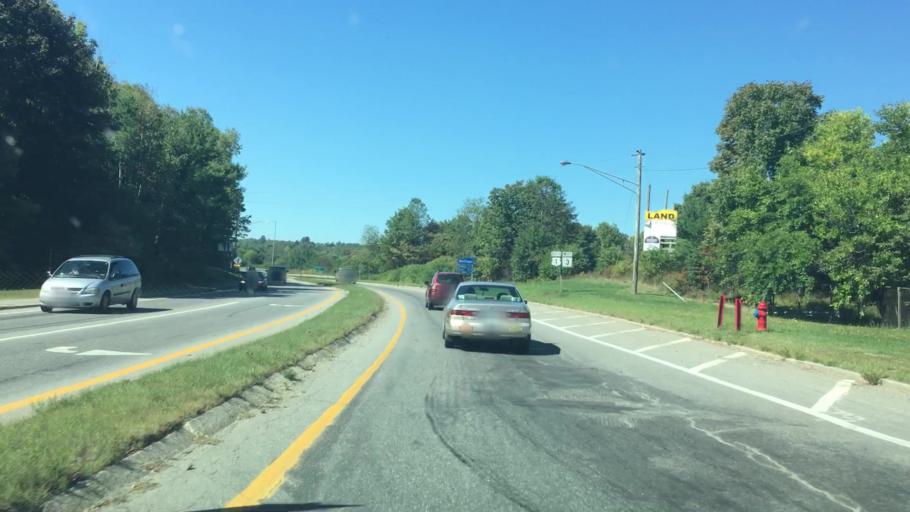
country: US
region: Maine
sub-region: Waldo County
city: Belfast
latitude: 44.4344
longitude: -69.0048
